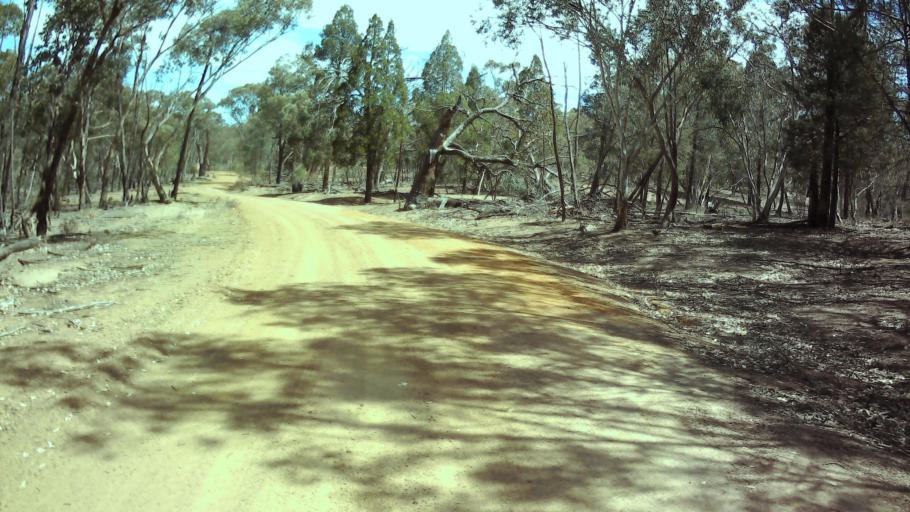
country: AU
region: New South Wales
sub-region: Weddin
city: Grenfell
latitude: -33.7996
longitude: 148.1597
